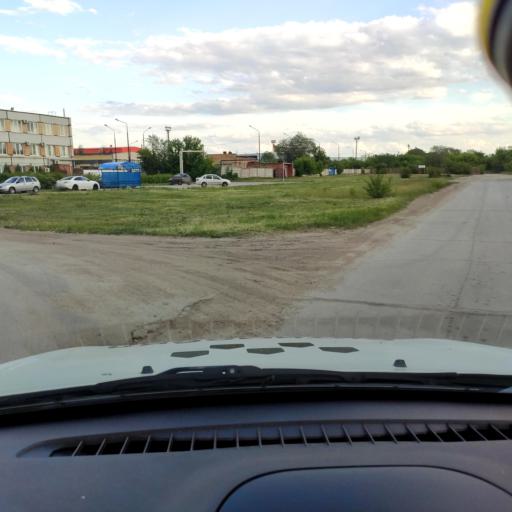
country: RU
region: Samara
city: Podstepki
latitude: 53.5786
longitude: 49.2284
